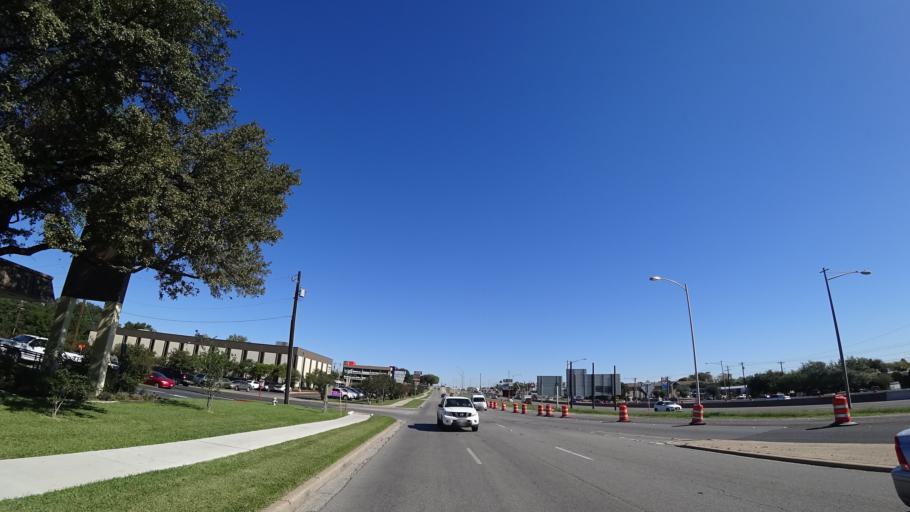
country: US
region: Texas
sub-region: Travis County
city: Austin
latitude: 30.2277
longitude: -97.7452
